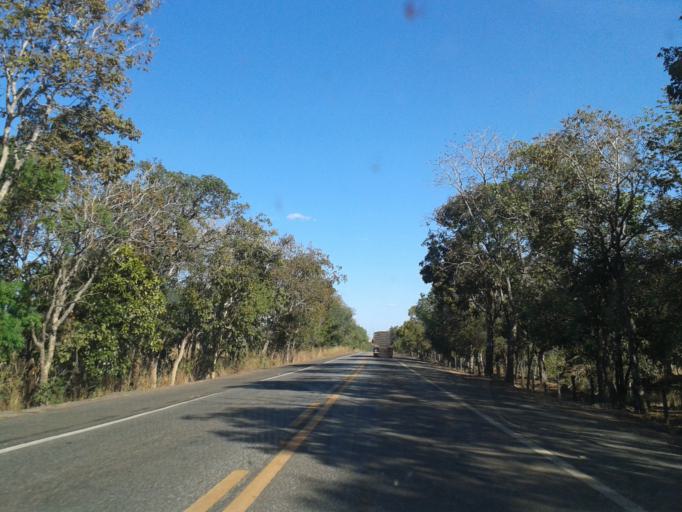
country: BR
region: Goias
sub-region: Mozarlandia
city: Mozarlandia
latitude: -14.8117
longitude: -50.5323
